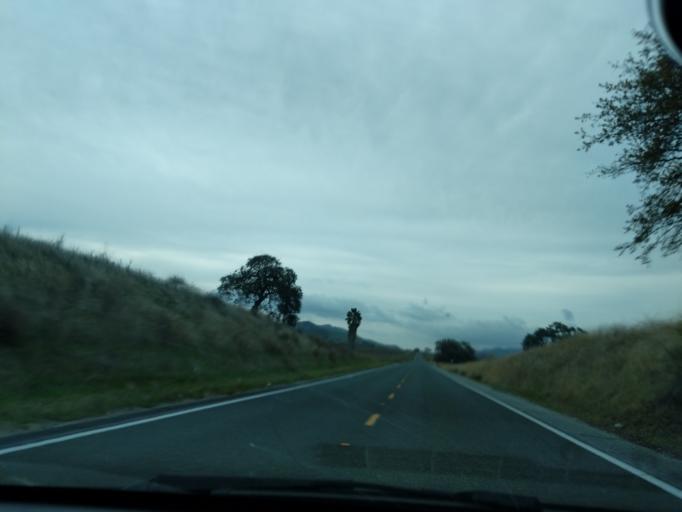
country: US
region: California
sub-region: San Benito County
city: Ridgemark
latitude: 36.6844
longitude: -121.2616
